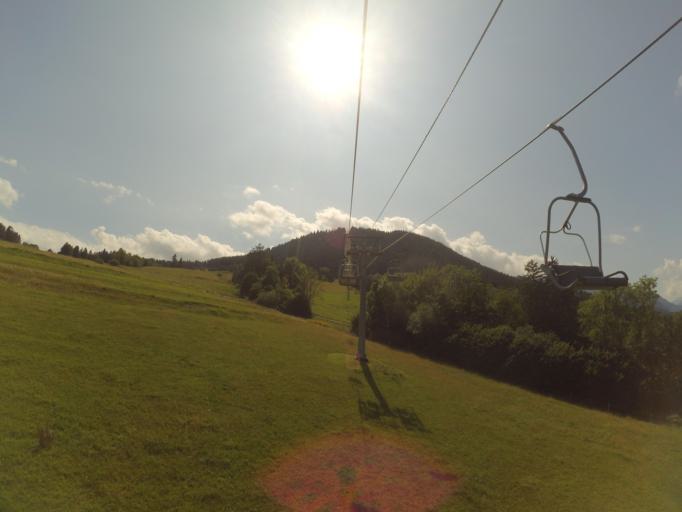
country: DE
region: Bavaria
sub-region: Swabia
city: Halblech
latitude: 47.6136
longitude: 10.8065
